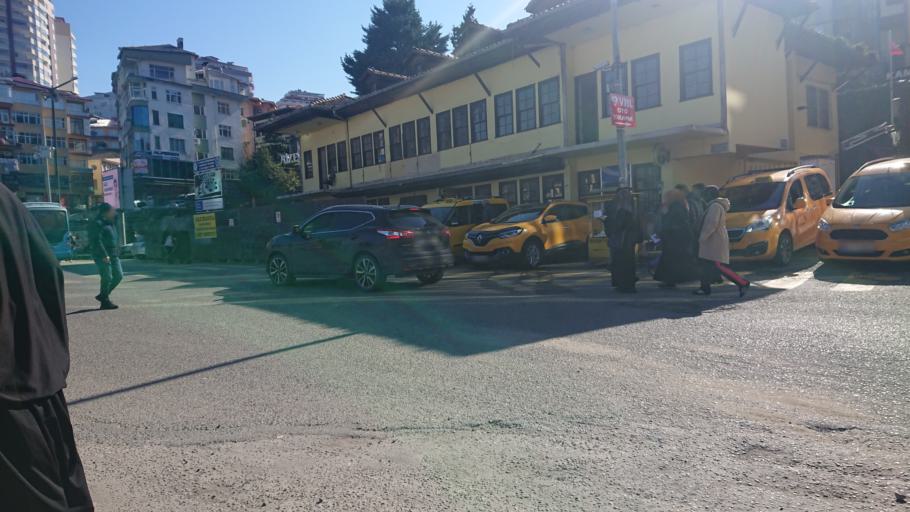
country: TR
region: Rize
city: Rize
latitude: 41.0254
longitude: 40.5160
